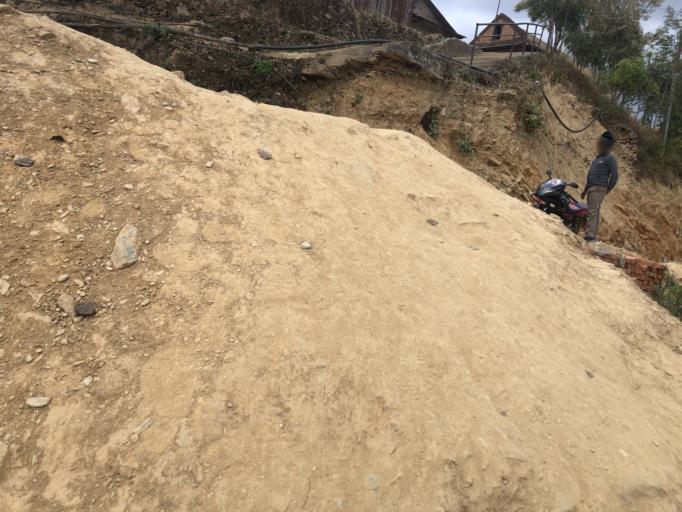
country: NP
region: Central Region
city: Banepa
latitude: 27.5569
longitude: 85.8025
